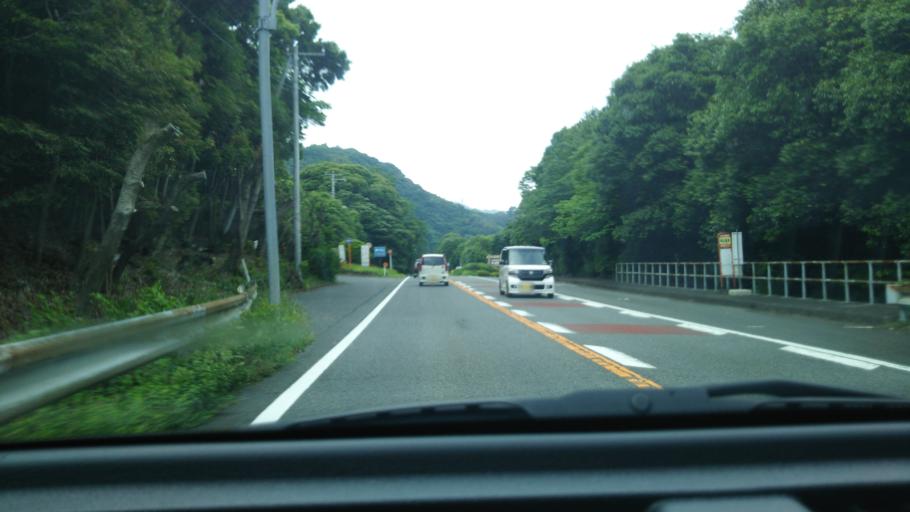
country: JP
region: Shizuoka
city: Ito
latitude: 34.8669
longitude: 139.0956
